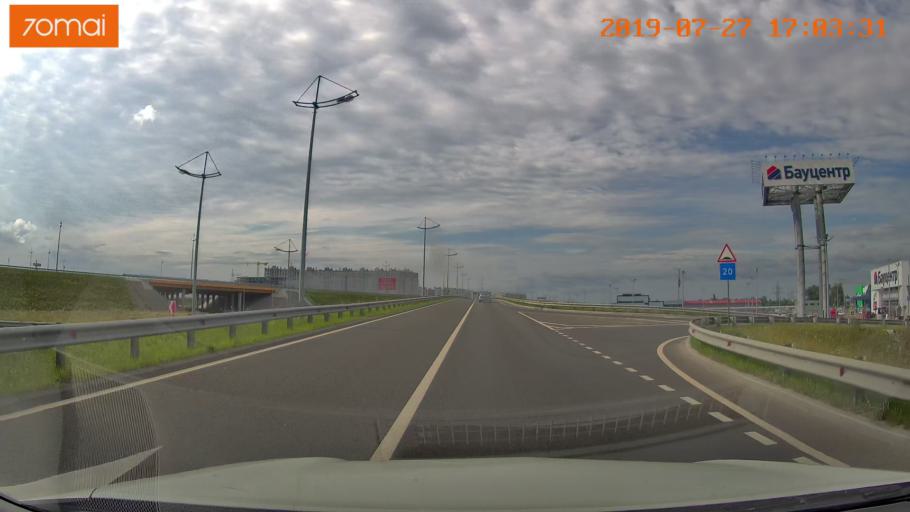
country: RU
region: Kaliningrad
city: Bol'shoe Isakovo
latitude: 54.7054
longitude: 20.6012
